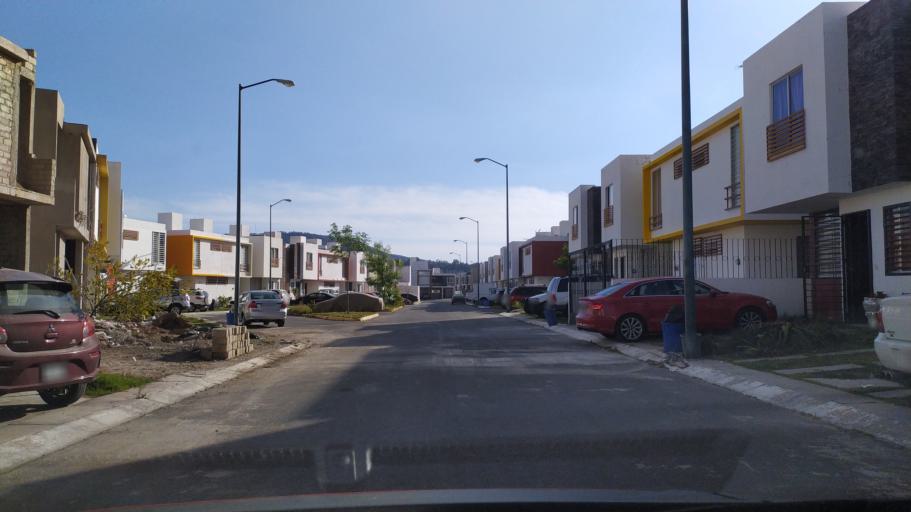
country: MX
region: Jalisco
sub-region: Tlajomulco de Zuniga
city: Palomar
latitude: 20.6324
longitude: -103.4805
